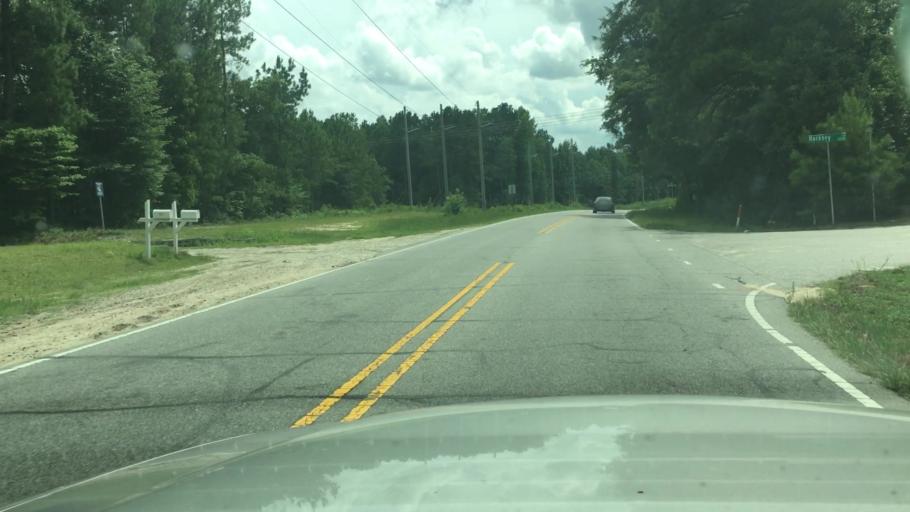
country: US
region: North Carolina
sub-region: Hoke County
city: Rockfish
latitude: 35.0128
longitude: -79.0118
